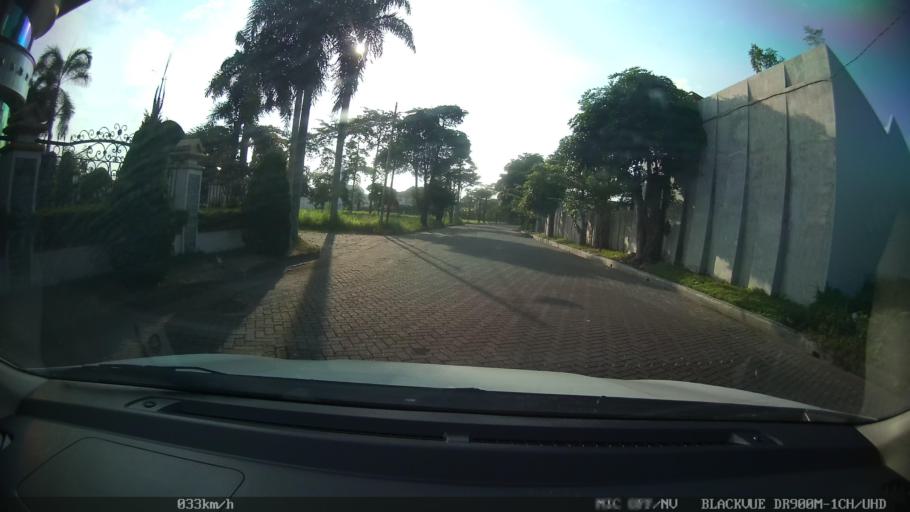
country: ID
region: North Sumatra
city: Medan
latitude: 3.6204
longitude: 98.6523
